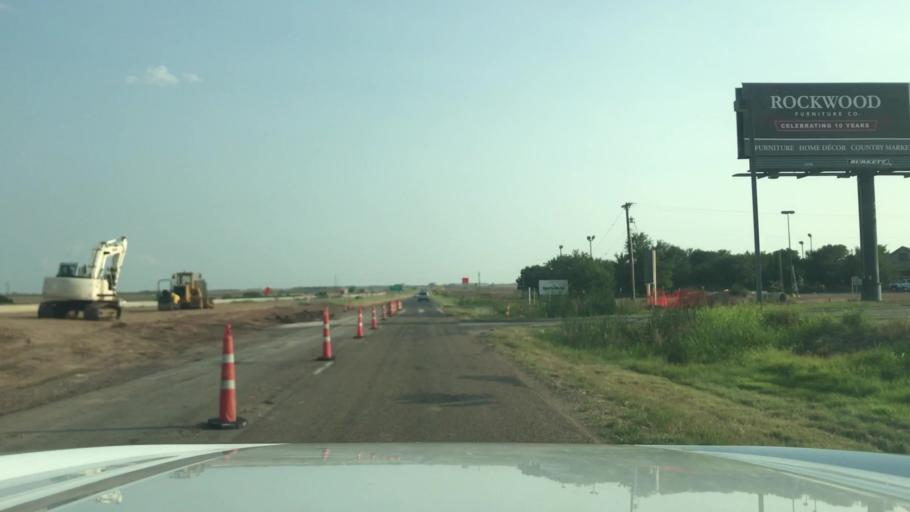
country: US
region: Texas
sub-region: Randall County
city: Canyon
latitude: 35.1135
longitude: -101.9109
